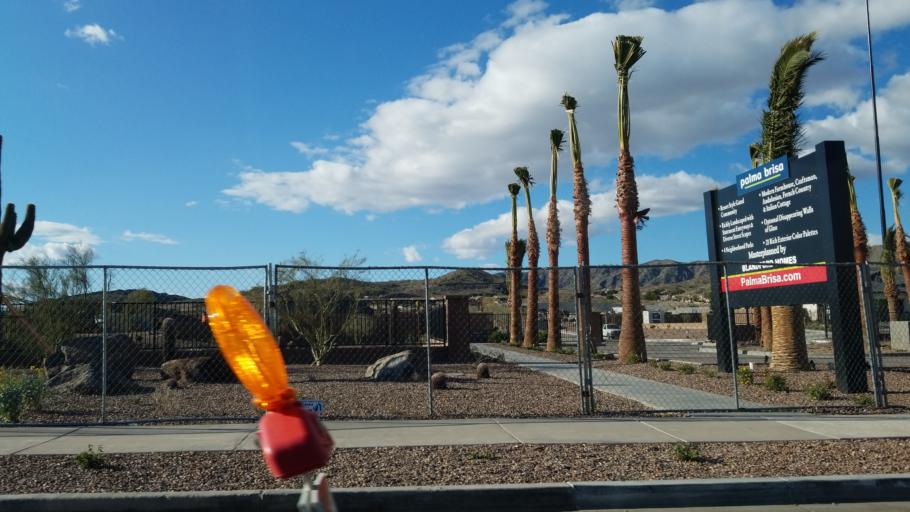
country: US
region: Arizona
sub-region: Maricopa County
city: Guadalupe
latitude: 33.2954
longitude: -112.0628
